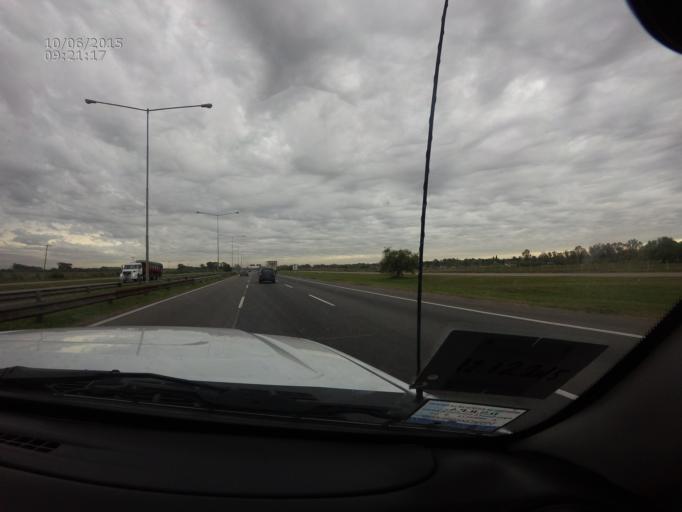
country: AR
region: Buenos Aires
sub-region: Partido de Campana
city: Campana
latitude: -34.2369
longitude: -58.9108
